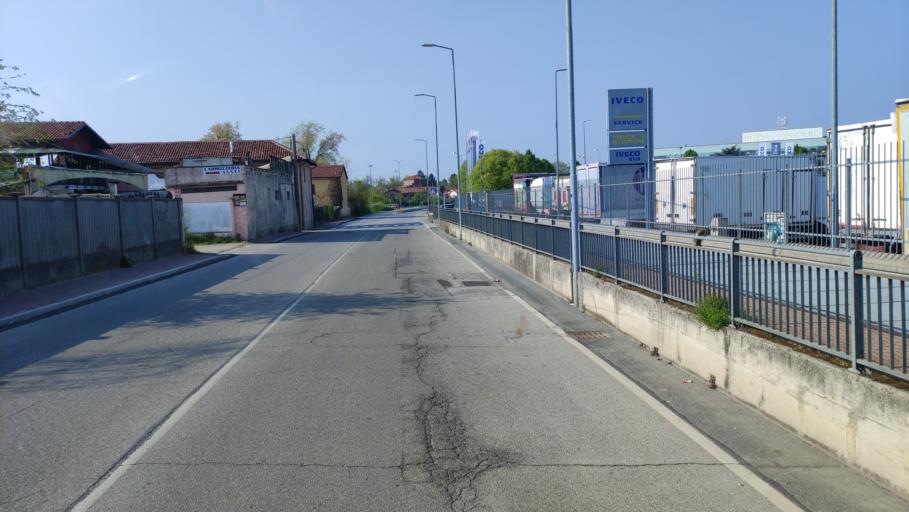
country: IT
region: Piedmont
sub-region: Provincia di Torino
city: Moncalieri
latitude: 44.9910
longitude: 7.7050
